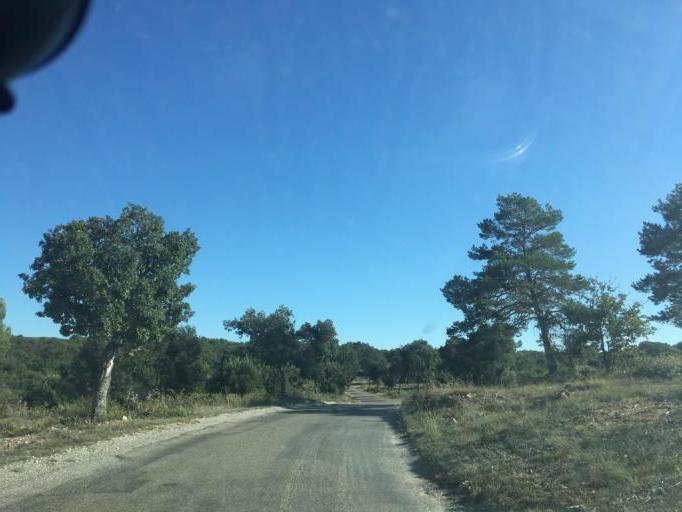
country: FR
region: Provence-Alpes-Cote d'Azur
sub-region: Departement des Alpes-de-Haute-Provence
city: Riez
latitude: 43.7366
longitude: 6.1002
